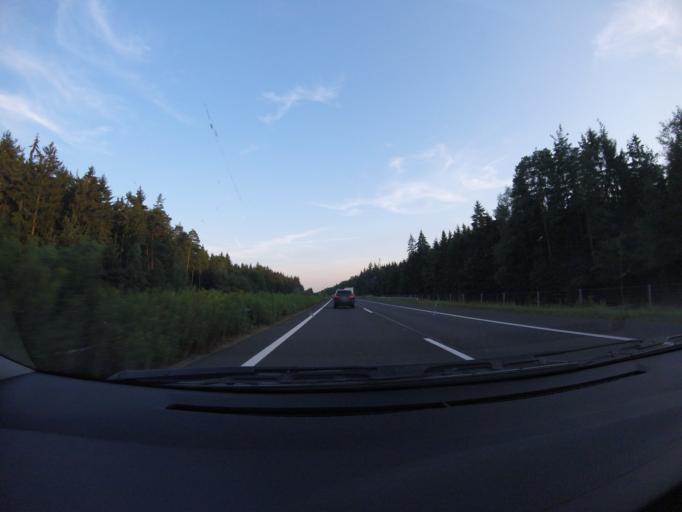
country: AT
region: Styria
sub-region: Politischer Bezirk Hartberg-Fuerstenfeld
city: Bad Waltersdorf
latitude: 47.1301
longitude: 15.9851
